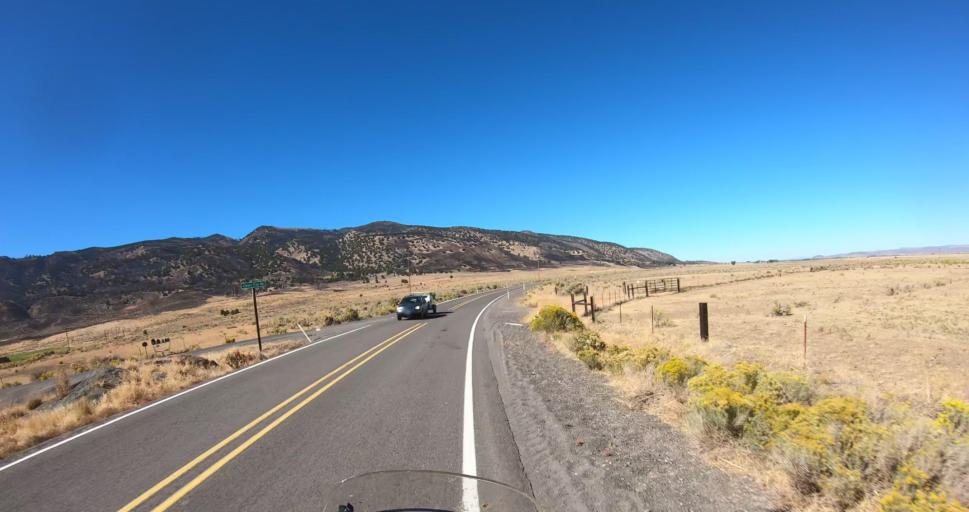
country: US
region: Oregon
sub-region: Lake County
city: Lakeview
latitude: 42.6200
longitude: -120.5045
